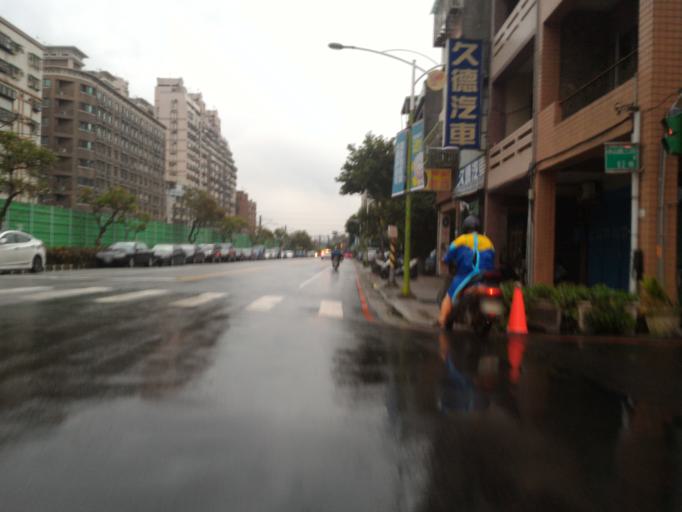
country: TW
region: Taipei
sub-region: Taipei
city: Banqiao
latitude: 24.9837
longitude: 121.4149
